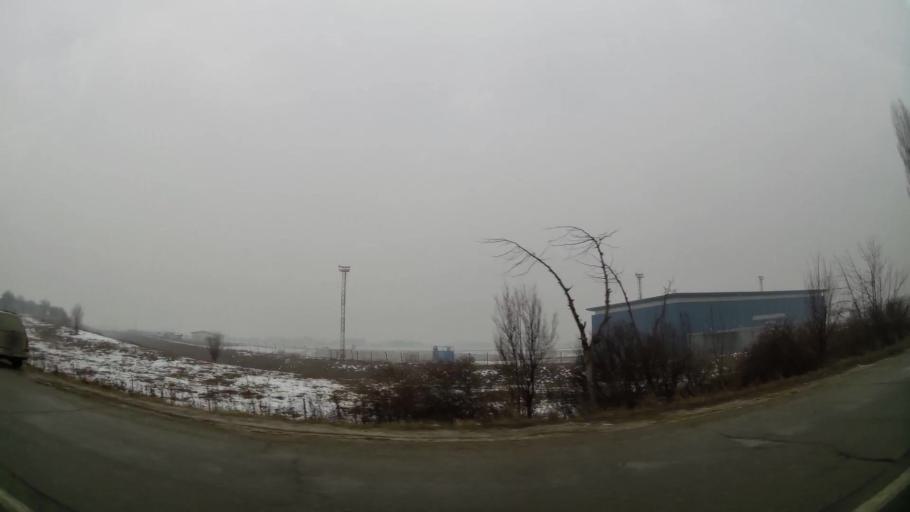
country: MK
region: Petrovec
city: Petrovec
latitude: 41.9526
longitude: 21.6307
